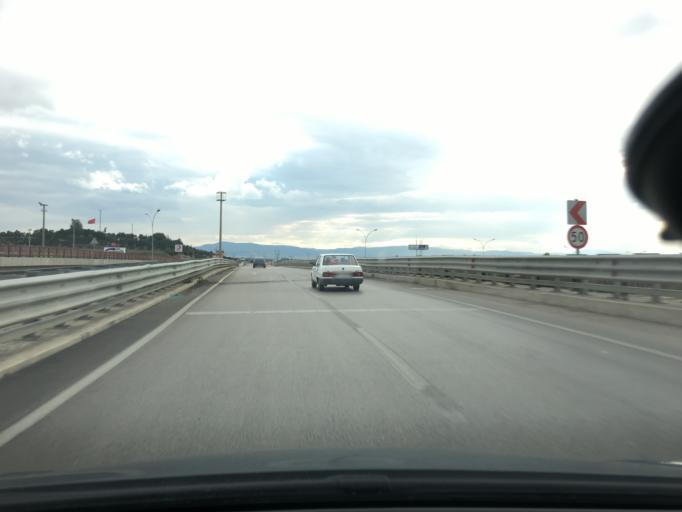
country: TR
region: Afyonkarahisar
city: Sincanli
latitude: 38.7971
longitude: 30.3903
